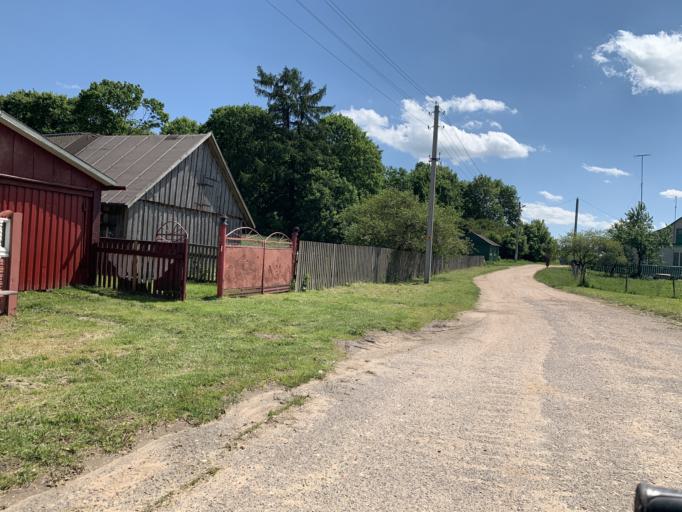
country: BY
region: Minsk
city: Kapyl'
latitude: 53.2574
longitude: 26.9531
